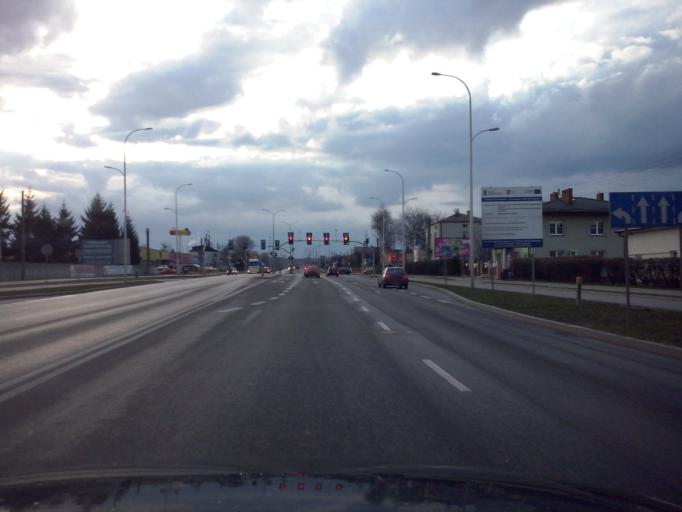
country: PL
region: Lublin Voivodeship
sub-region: Chelm
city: Chelm
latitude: 51.1446
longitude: 23.4578
